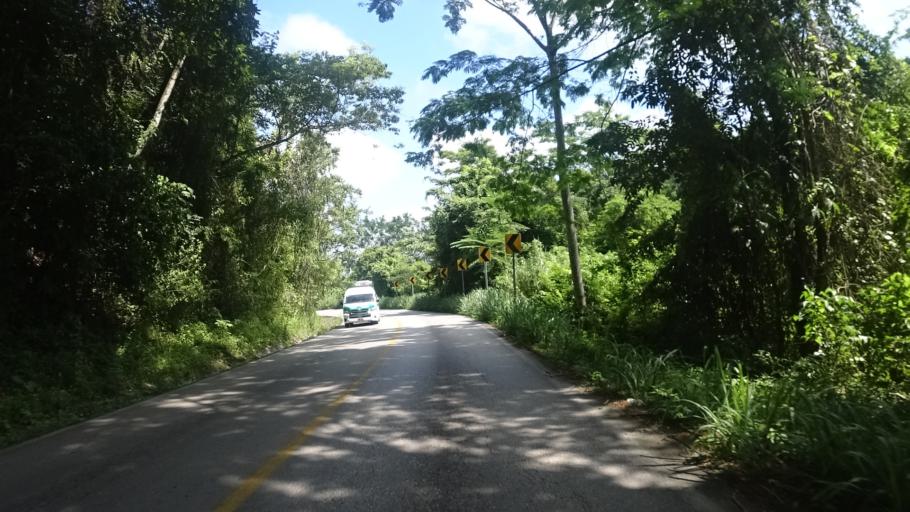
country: MX
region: Chiapas
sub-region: Palenque
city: Doctor Samuel Leon Brindis
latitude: 17.4636
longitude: -91.9627
